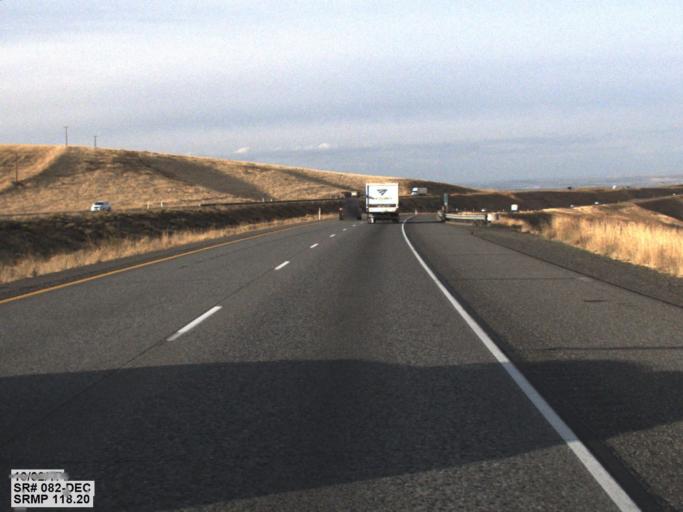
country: US
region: Washington
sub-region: Benton County
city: Highland
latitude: 46.0911
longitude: -119.2228
